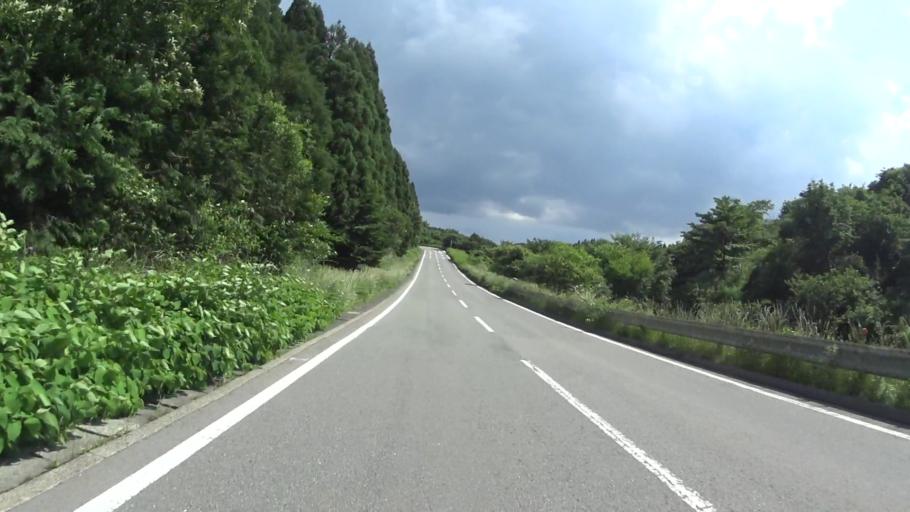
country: JP
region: Kumamoto
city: Aso
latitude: 33.0449
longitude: 131.1666
